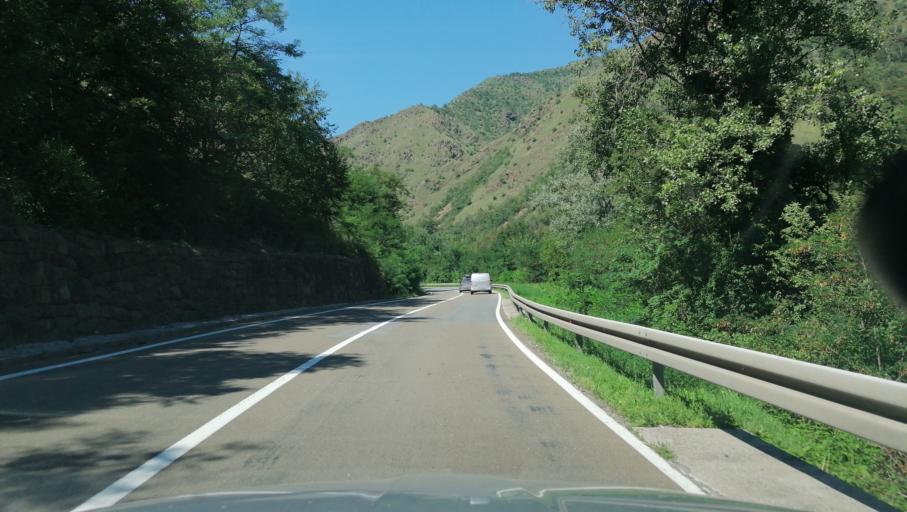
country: RS
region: Central Serbia
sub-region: Raski Okrug
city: Kraljevo
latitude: 43.5782
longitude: 20.5865
